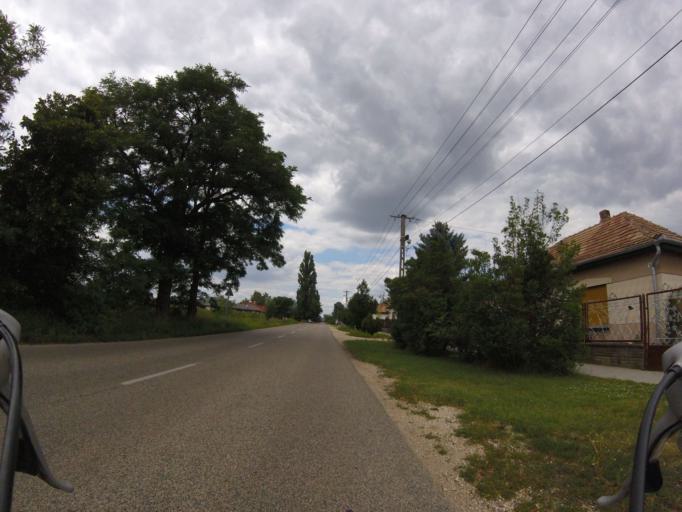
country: HU
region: Fejer
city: Pakozd
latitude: 47.1690
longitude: 18.5708
